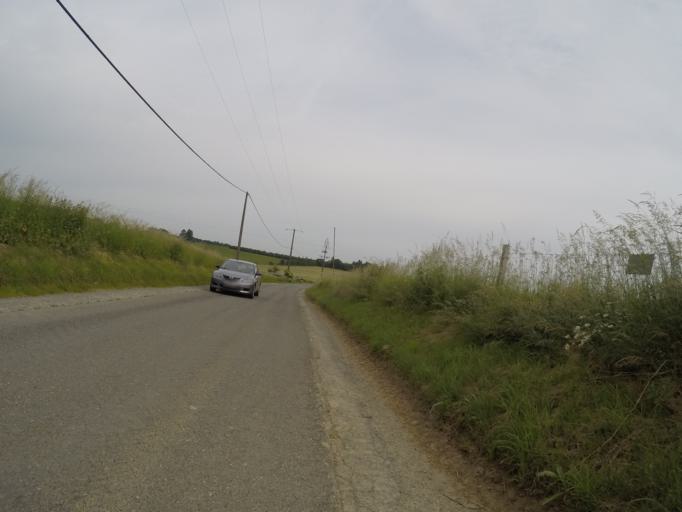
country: BE
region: Wallonia
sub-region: Province de Namur
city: Dinant
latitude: 50.2873
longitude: 4.9645
